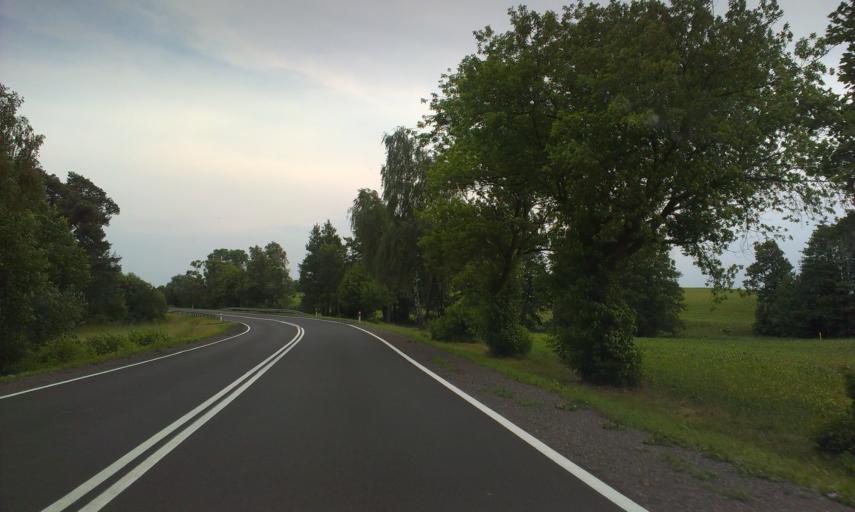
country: PL
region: West Pomeranian Voivodeship
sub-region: Powiat szczecinecki
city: Szczecinek
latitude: 53.7601
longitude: 16.6478
